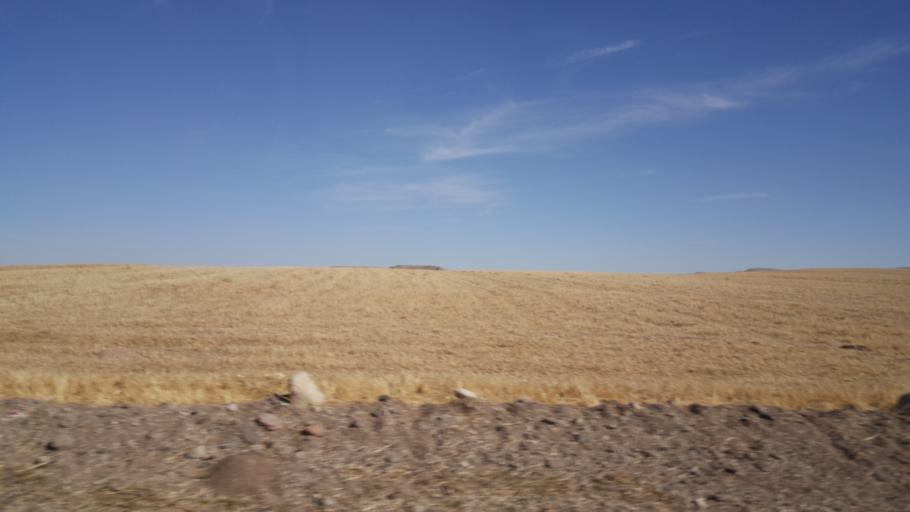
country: TR
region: Ankara
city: Yenice
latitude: 39.3247
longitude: 32.7549
